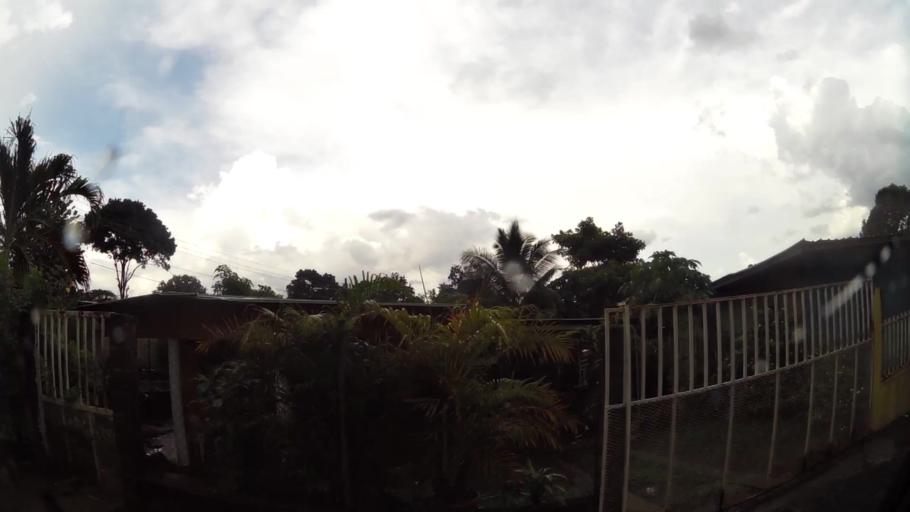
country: PA
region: Panama
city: Cabra Numero Uno
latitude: 9.1005
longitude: -79.3247
